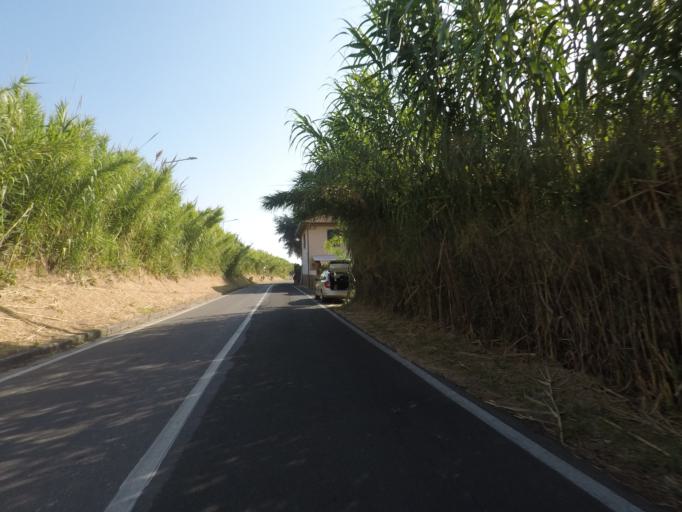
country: IT
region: Liguria
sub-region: Provincia di La Spezia
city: Casano-Dogana-Isola
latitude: 44.0611
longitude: 10.0298
